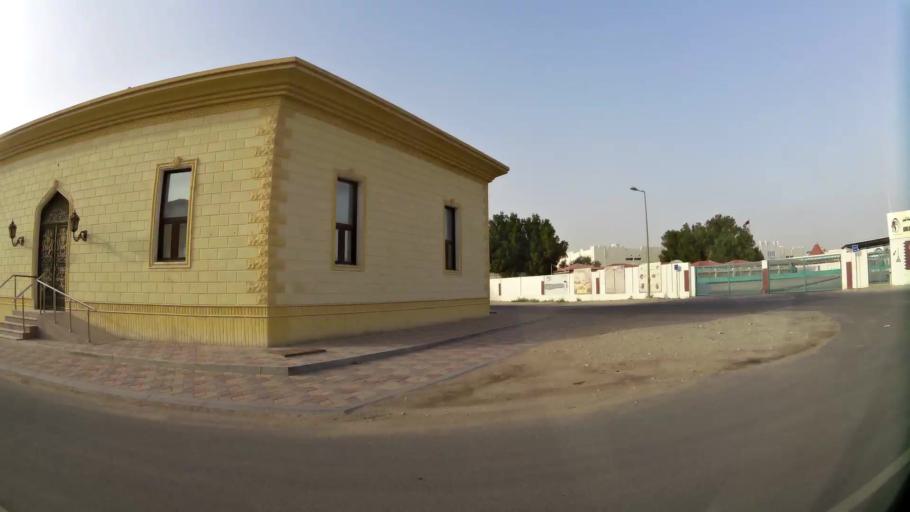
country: QA
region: Baladiyat ar Rayyan
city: Ar Rayyan
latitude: 25.2451
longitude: 51.4515
